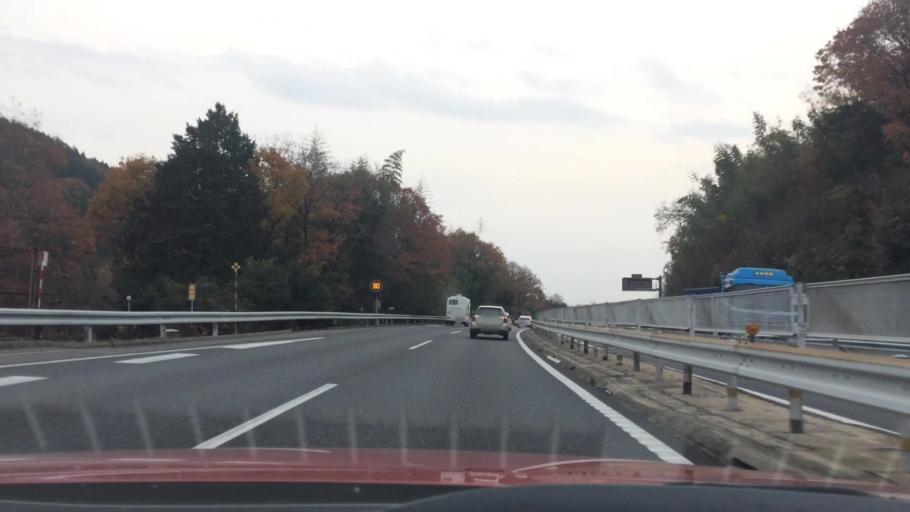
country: JP
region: Aichi
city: Kasugai
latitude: 35.3260
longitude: 137.0239
